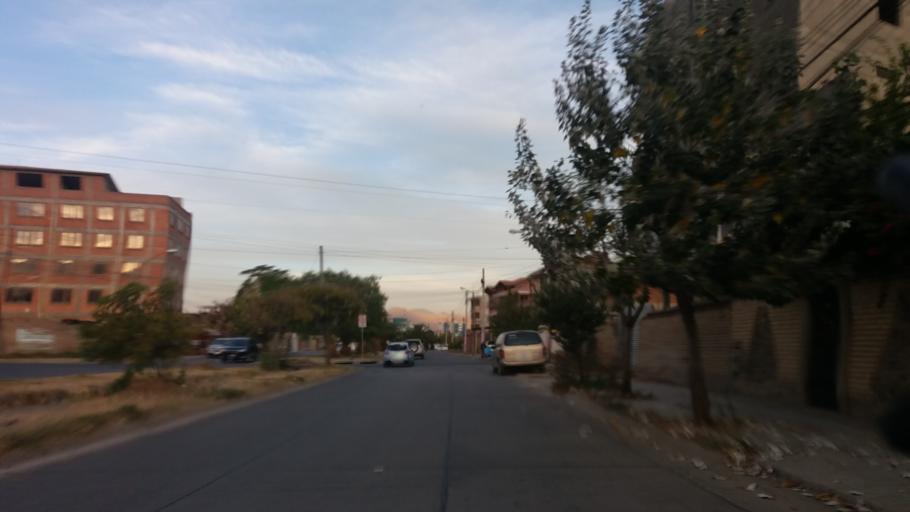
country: BO
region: Cochabamba
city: Cochabamba
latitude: -17.3772
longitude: -66.1911
